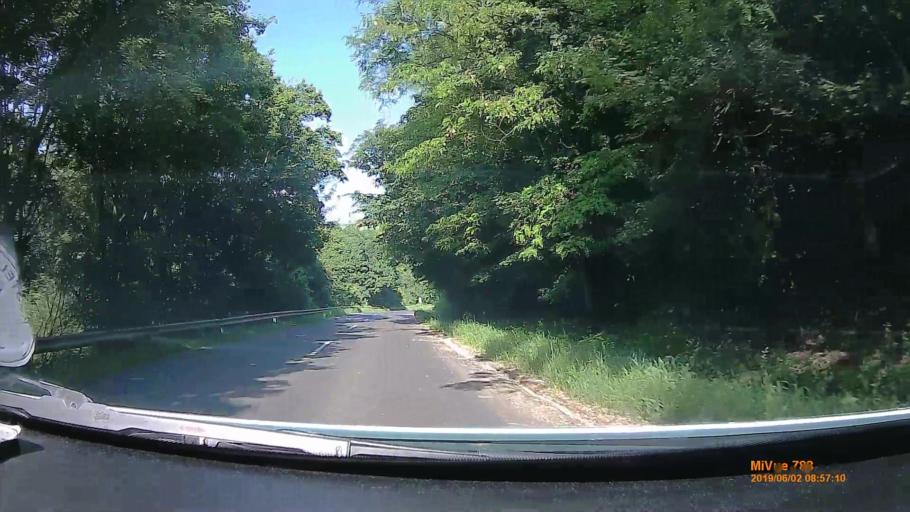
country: HU
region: Borsod-Abauj-Zemplen
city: Sajobabony
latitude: 48.1553
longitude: 20.6436
